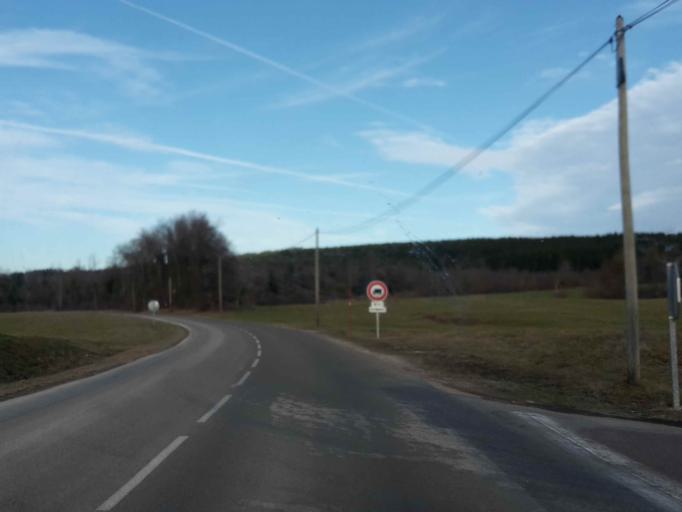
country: FR
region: Franche-Comte
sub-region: Departement du Doubs
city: Valdahon
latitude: 47.1427
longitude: 6.3749
